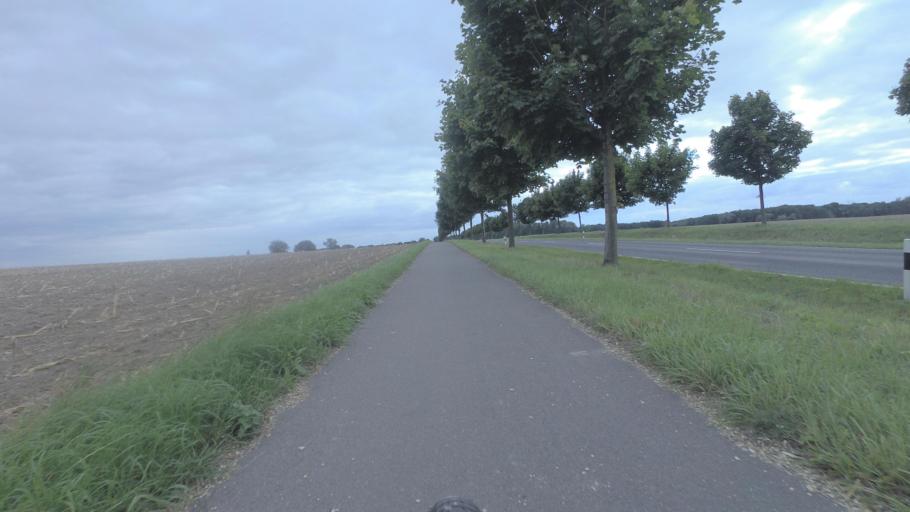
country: DE
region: Brandenburg
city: Werneuchen
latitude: 52.6065
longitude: 13.6839
